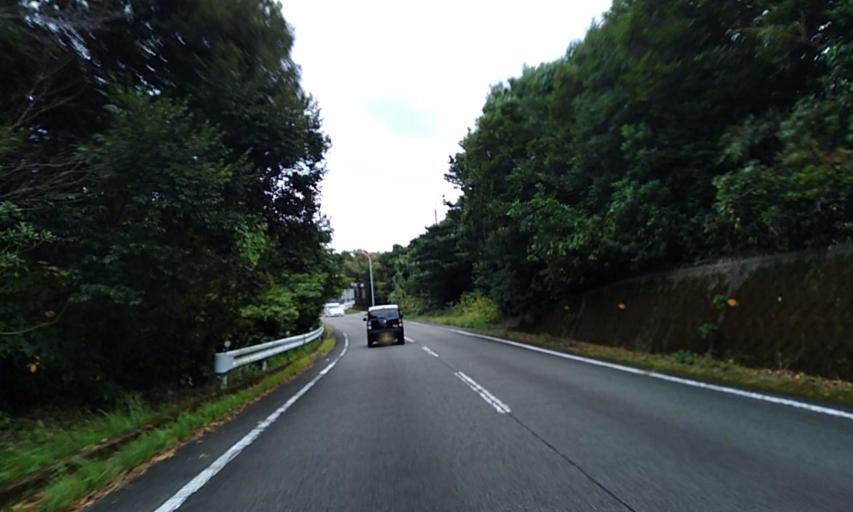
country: JP
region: Wakayama
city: Shingu
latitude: 33.4687
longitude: 135.8530
